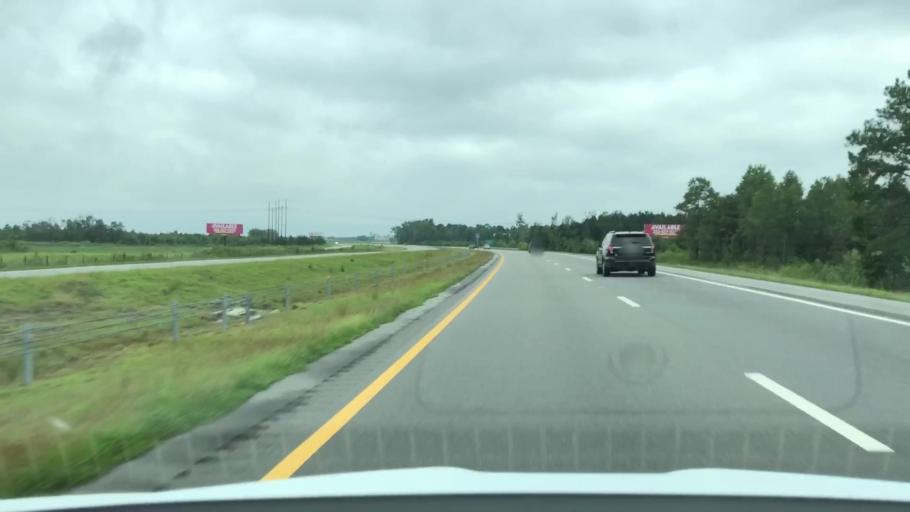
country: US
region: North Carolina
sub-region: Wayne County
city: Elroy
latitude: 35.3964
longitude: -77.8691
